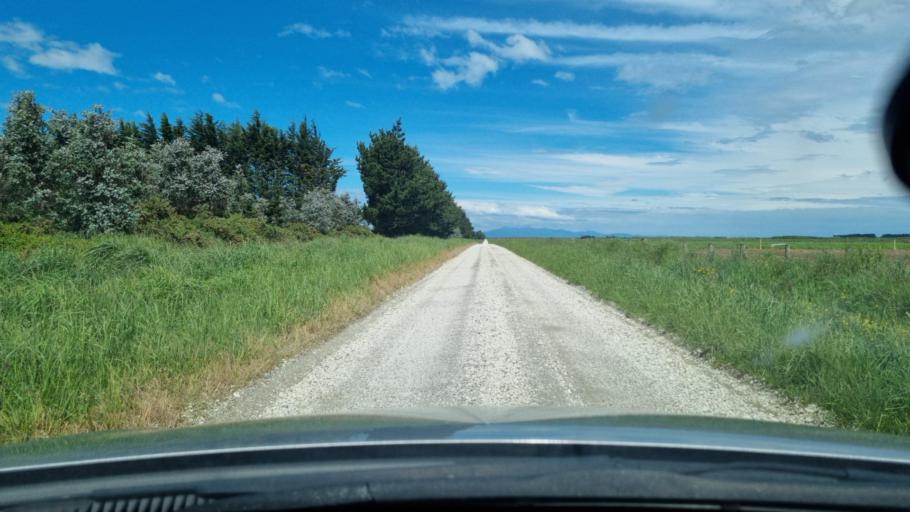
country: NZ
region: Southland
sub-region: Invercargill City
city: Invercargill
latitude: -46.3727
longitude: 168.2768
